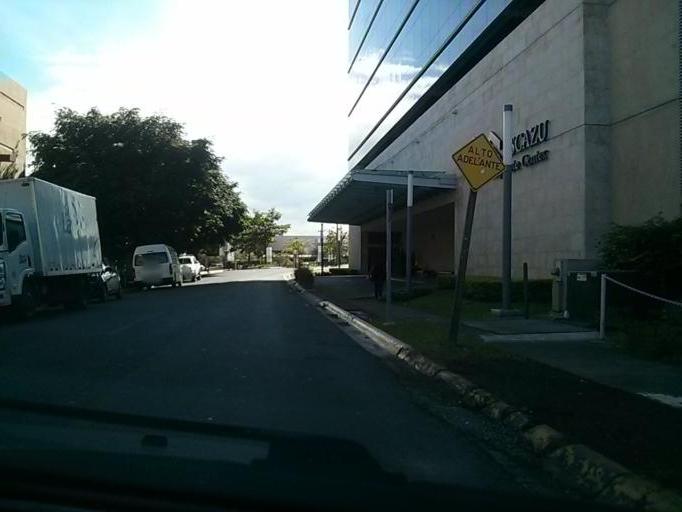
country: CR
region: San Jose
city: San Rafael
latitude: 9.9435
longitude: -84.1512
